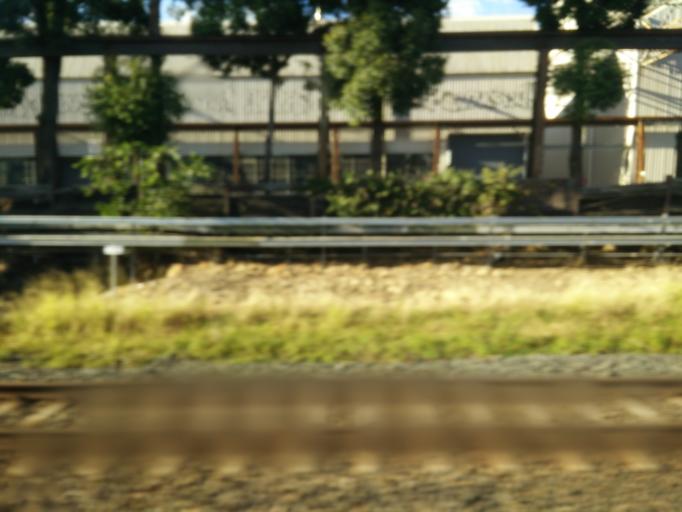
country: AU
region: New South Wales
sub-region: Marrickville
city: Newtown
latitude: -33.9096
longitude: 151.1739
